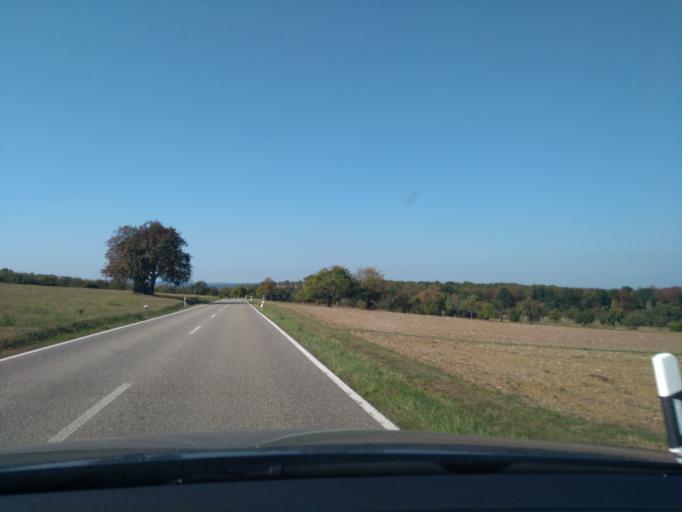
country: DE
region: Baden-Wuerttemberg
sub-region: Karlsruhe Region
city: Birkenfeld
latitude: 48.8710
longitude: 8.6142
